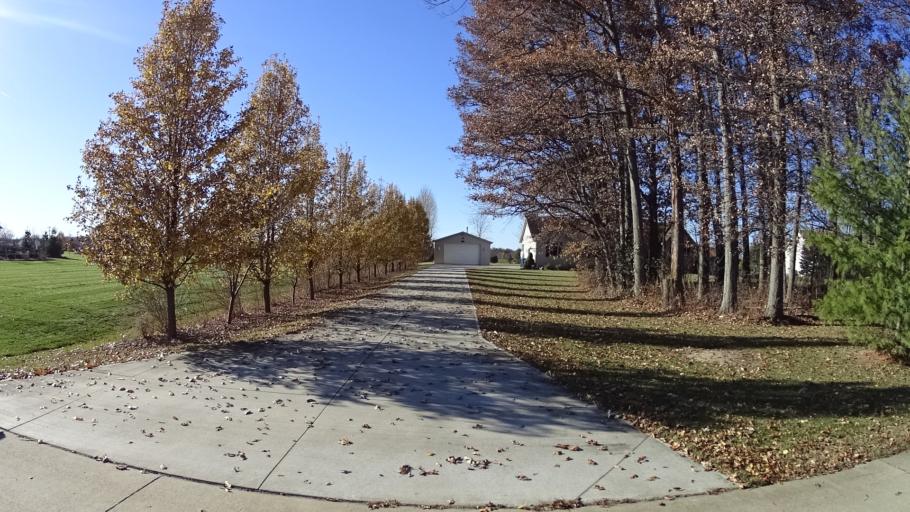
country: US
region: Ohio
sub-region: Lorain County
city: Lagrange
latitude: 41.3015
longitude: -82.1144
